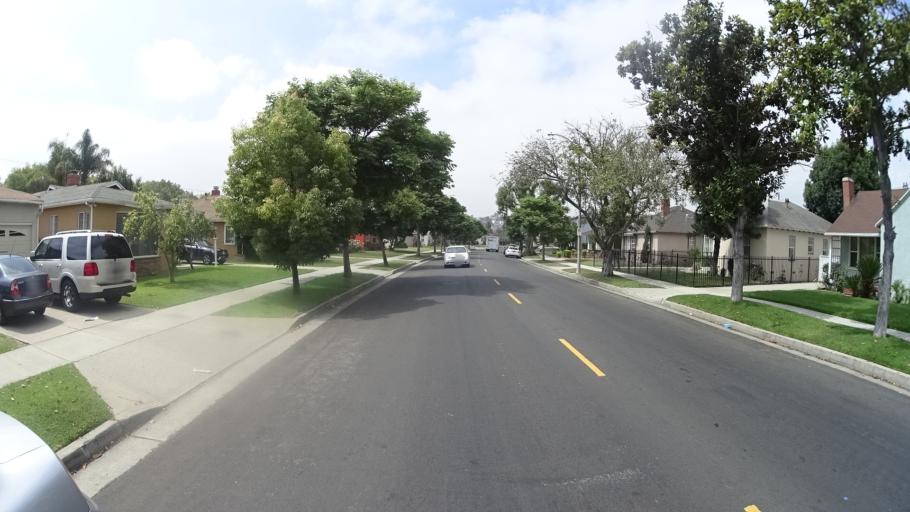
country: US
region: California
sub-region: Los Angeles County
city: View Park-Windsor Hills
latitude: 34.0171
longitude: -118.3404
